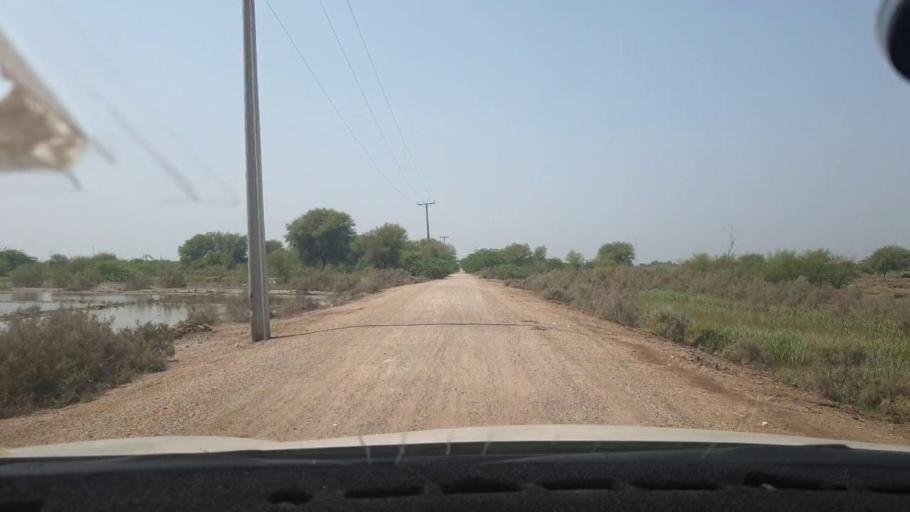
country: PK
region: Sindh
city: Tando Mittha Khan
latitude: 25.9208
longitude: 69.2510
